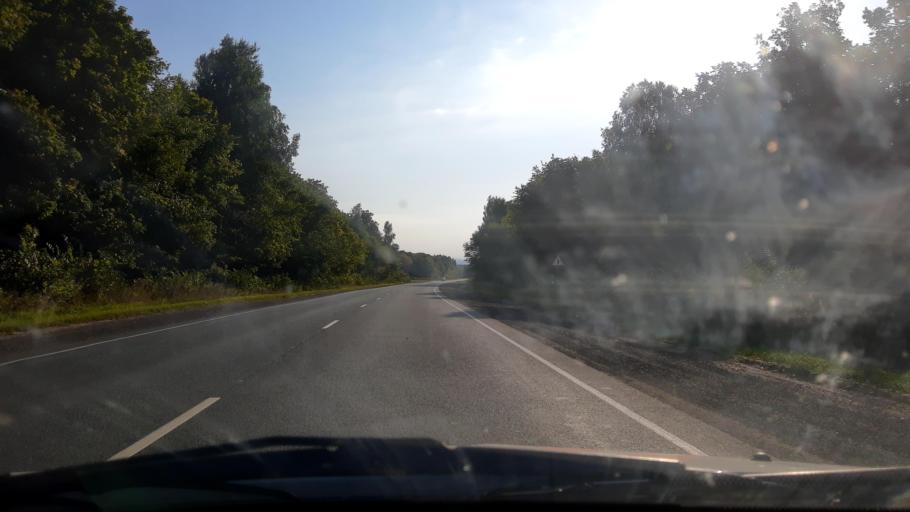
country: RU
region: Bashkortostan
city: Oktyabr'skiy
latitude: 54.4443
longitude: 53.5486
